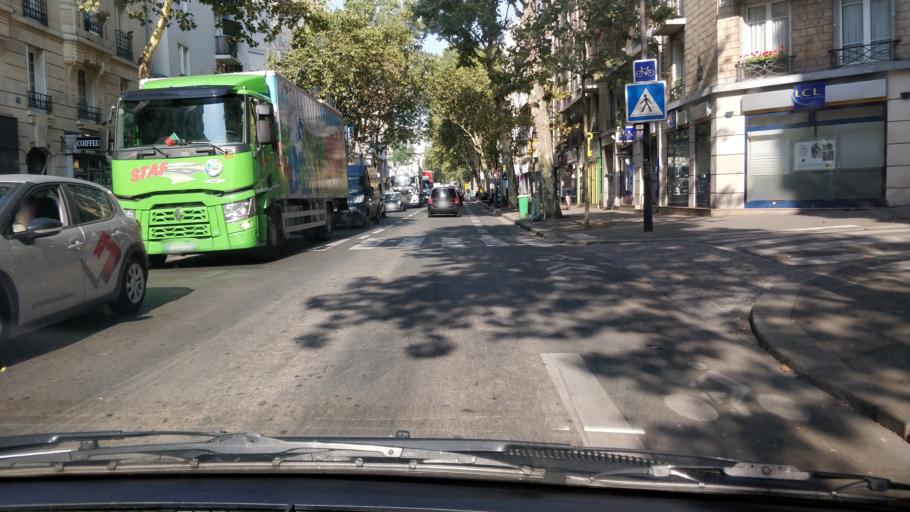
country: FR
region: Ile-de-France
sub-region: Departement de Seine-Saint-Denis
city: Bagnolet
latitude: 48.8646
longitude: 2.4075
